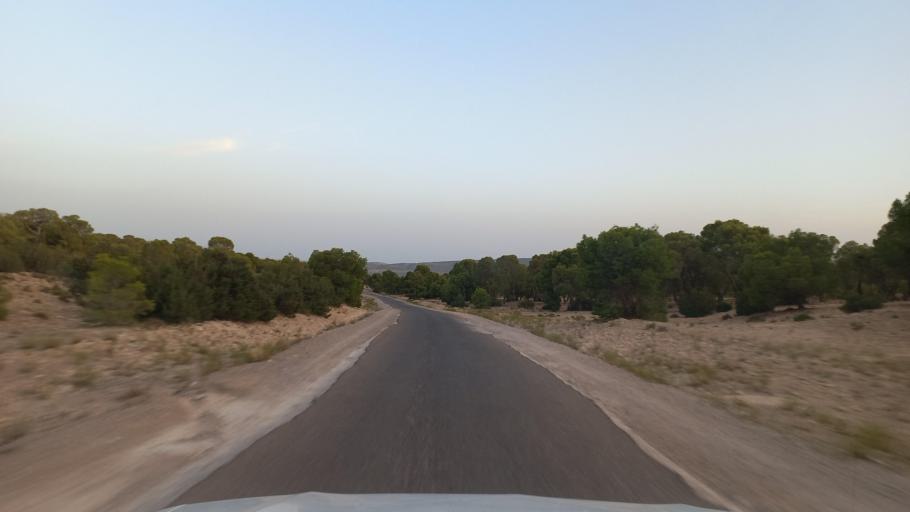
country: TN
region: Al Qasrayn
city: Sbiba
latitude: 35.4242
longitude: 8.9219
